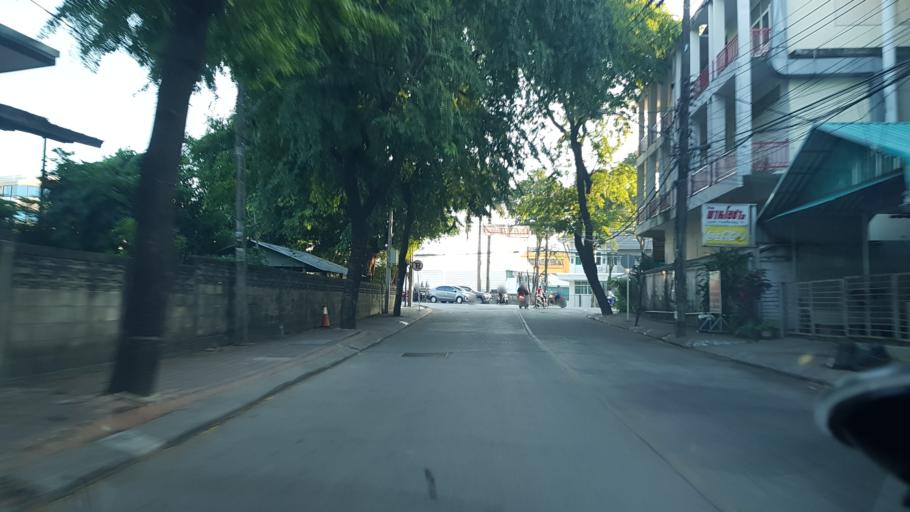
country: TH
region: Chiang Rai
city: Chiang Rai
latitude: 19.9072
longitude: 99.8355
